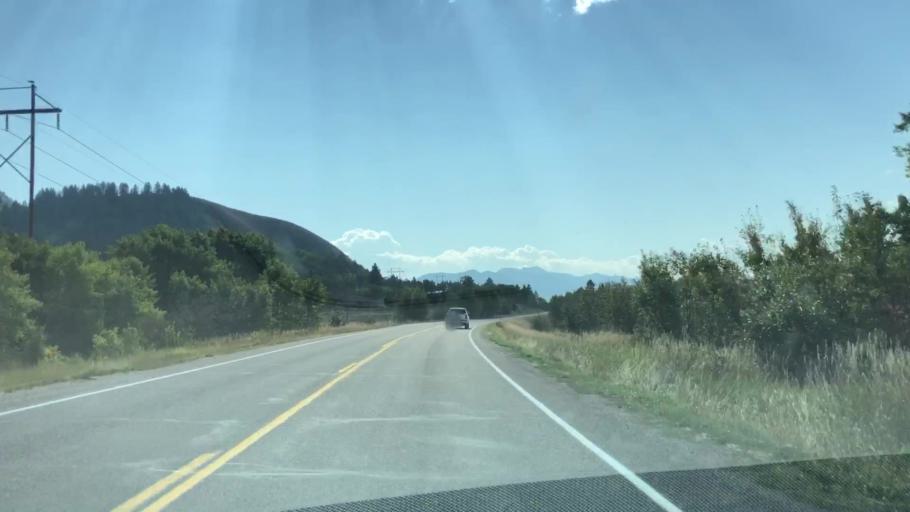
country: US
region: Wyoming
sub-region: Teton County
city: Hoback
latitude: 43.2153
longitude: -111.0632
